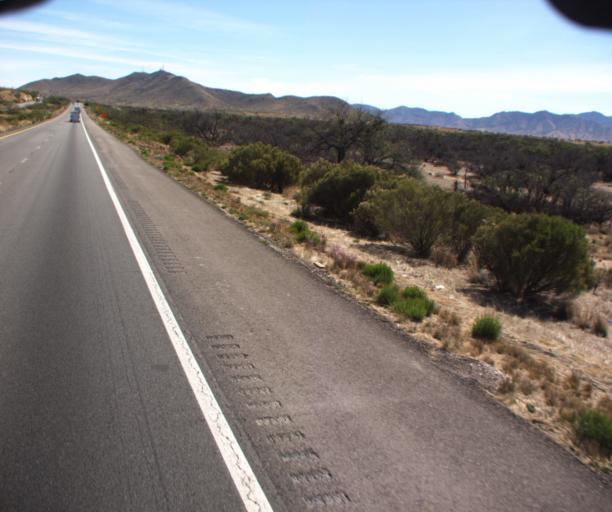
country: US
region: Arizona
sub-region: Cochise County
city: Saint David
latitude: 32.0056
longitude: -110.1403
